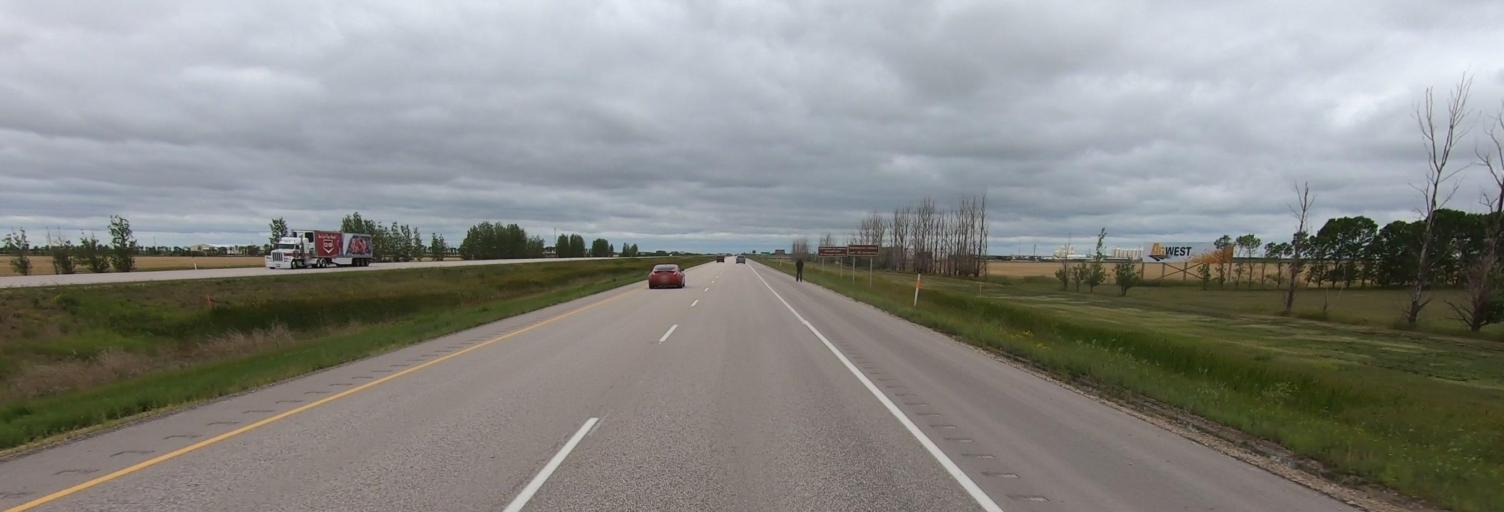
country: CA
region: Manitoba
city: Headingley
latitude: 49.9095
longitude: -97.7711
